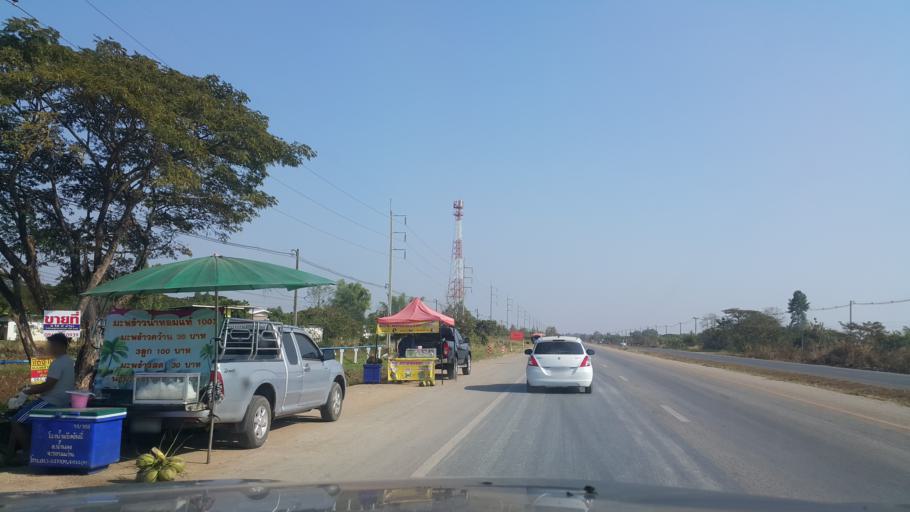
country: TH
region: Khon Kaen
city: Khon Kaen
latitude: 16.5068
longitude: 102.8672
